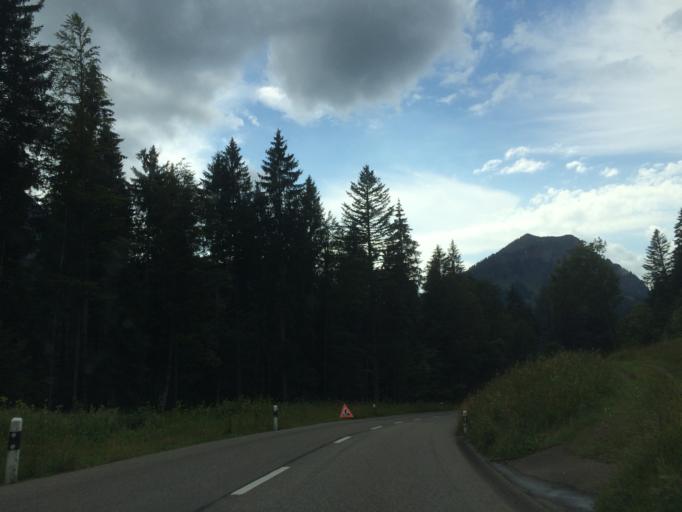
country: CH
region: Appenzell Ausserrhoden
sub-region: Bezirk Hinterland
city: Urnasch
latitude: 47.2471
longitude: 9.2819
